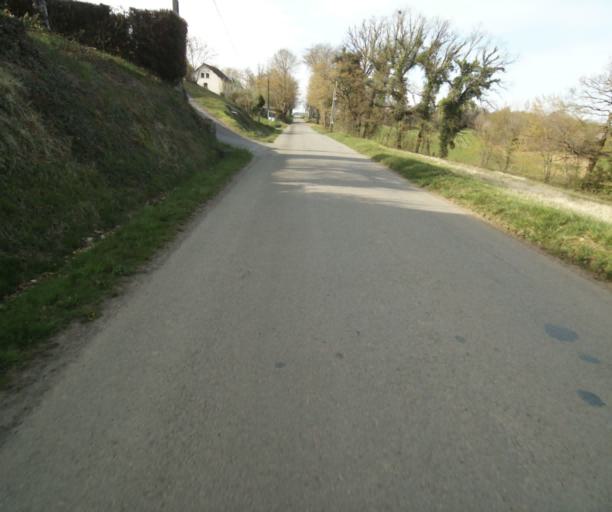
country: FR
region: Limousin
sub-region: Departement de la Correze
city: Naves
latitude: 45.2980
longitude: 1.7401
